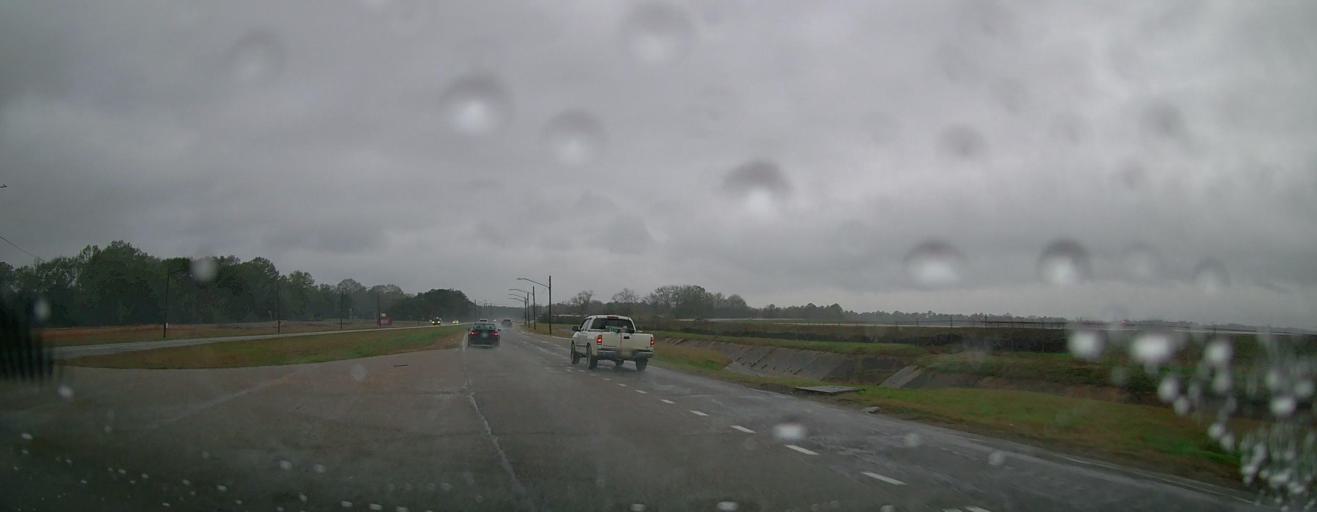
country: US
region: Alabama
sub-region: Montgomery County
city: Montgomery
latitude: 32.3692
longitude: -86.3556
